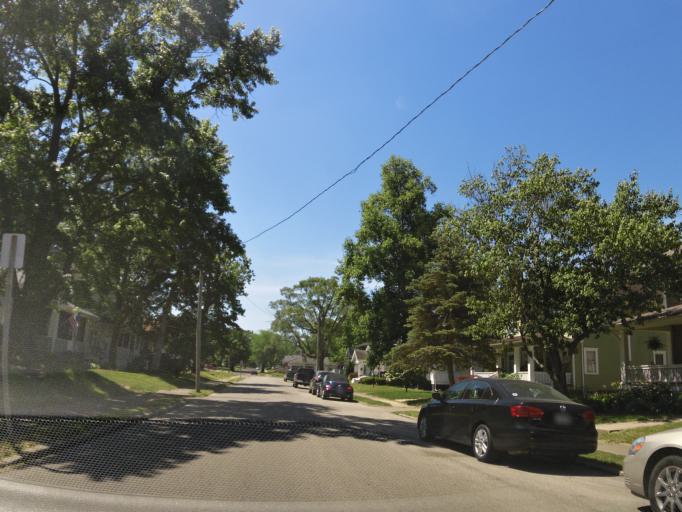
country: US
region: Illinois
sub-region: Vermilion County
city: Danville
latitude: 40.1469
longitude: -87.6330
